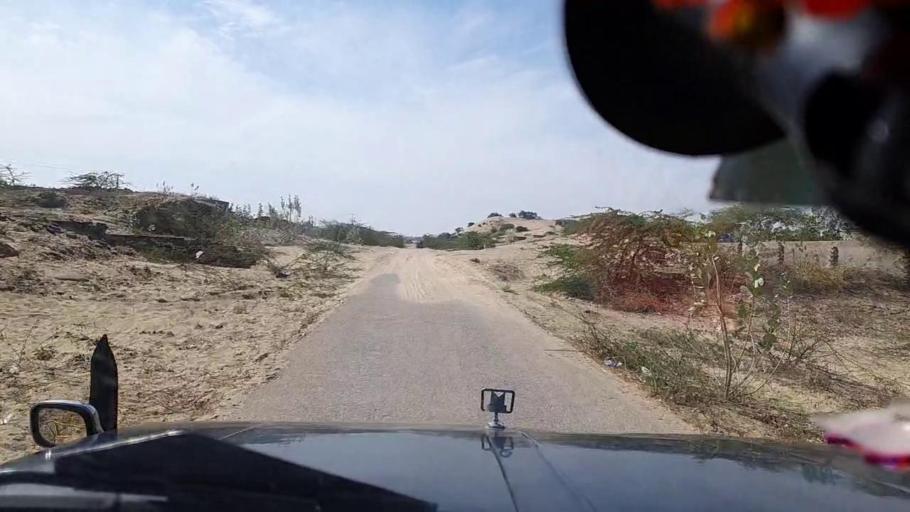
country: PK
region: Sindh
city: Diplo
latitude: 24.4577
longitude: 69.5796
